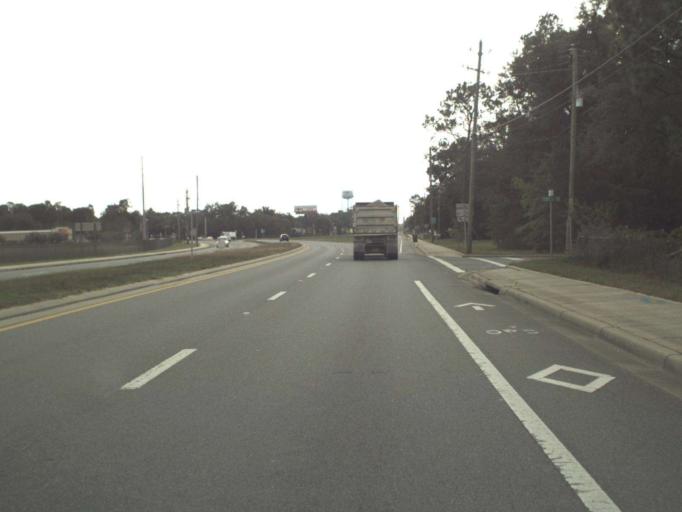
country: US
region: Florida
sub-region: Santa Rosa County
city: Point Baker
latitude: 30.6701
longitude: -87.0544
